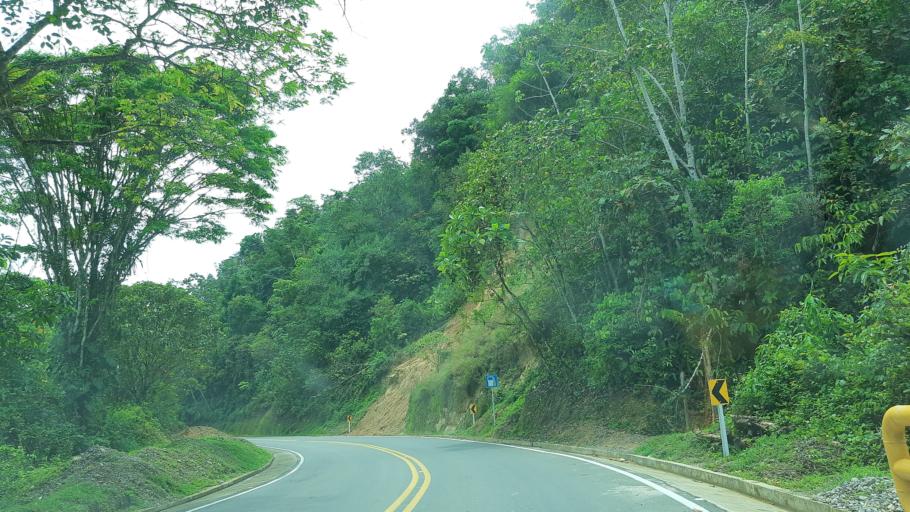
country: CO
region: Boyaca
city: San Luis de Gaceno
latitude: 4.8309
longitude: -73.1564
